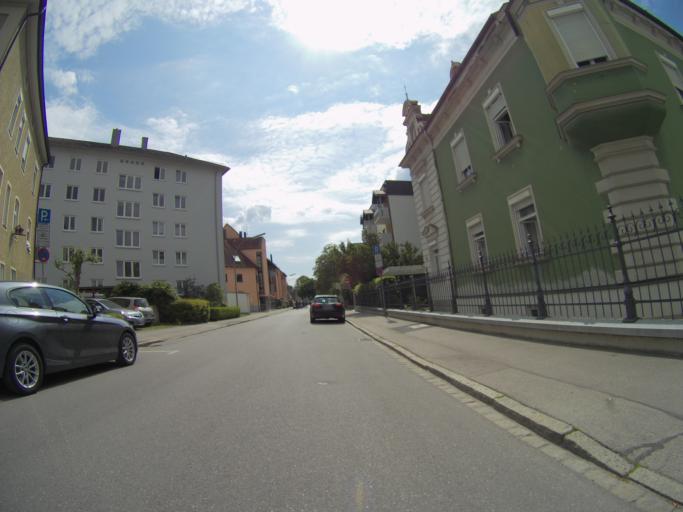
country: DE
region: Bavaria
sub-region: Upper Bavaria
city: Freising
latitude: 48.3970
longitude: 11.7425
